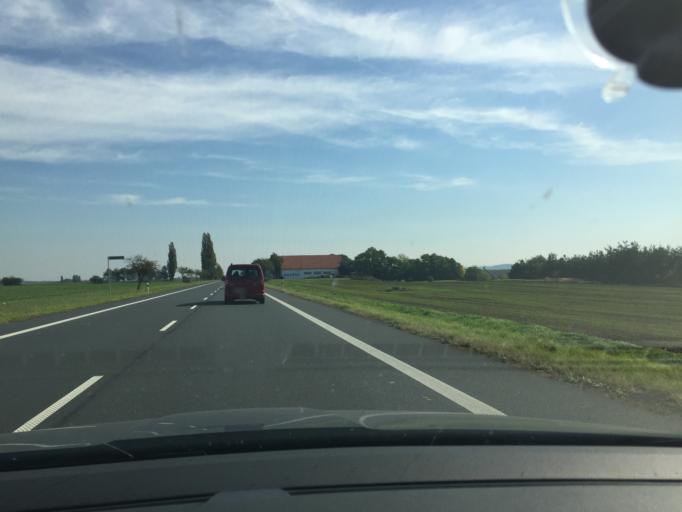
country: CZ
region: Central Bohemia
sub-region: Okres Kolin
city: Kourim
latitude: 50.0492
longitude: 14.9619
